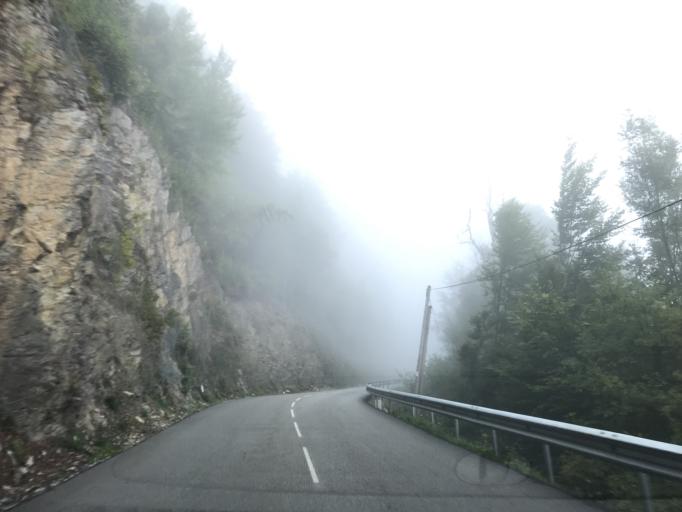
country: FR
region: Rhone-Alpes
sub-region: Departement de la Haute-Savoie
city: Talloires
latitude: 45.8117
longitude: 6.2428
